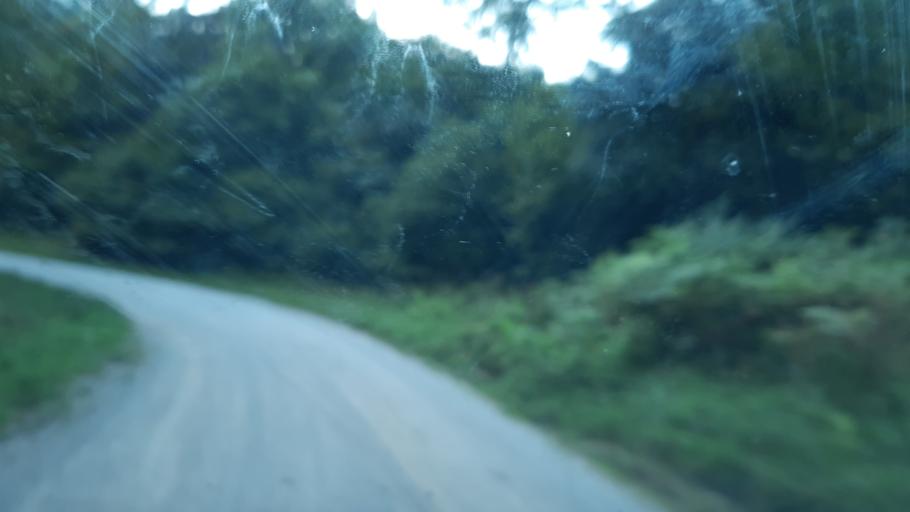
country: SI
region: Kocevje
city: Kocevje
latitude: 45.6680
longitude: 14.9543
